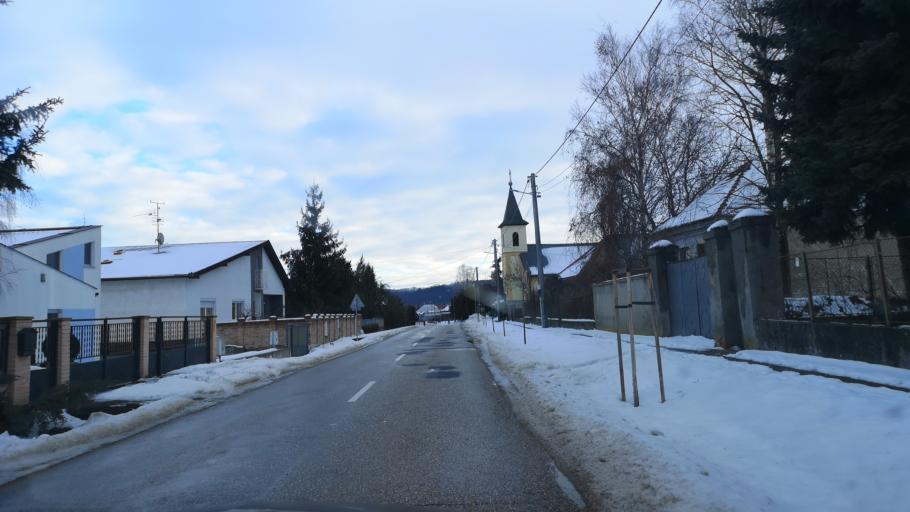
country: SK
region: Nitriansky
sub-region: Okres Nitra
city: Vrable
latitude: 48.1127
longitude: 18.3359
